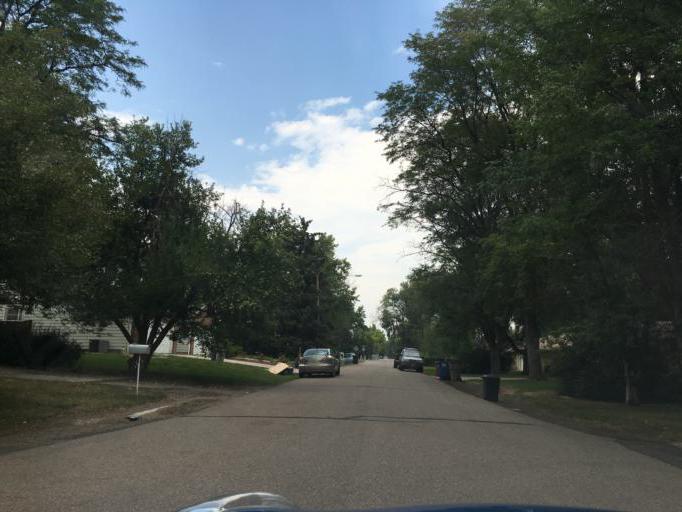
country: US
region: Colorado
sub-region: Jefferson County
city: Wheat Ridge
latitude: 39.7436
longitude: -105.0920
